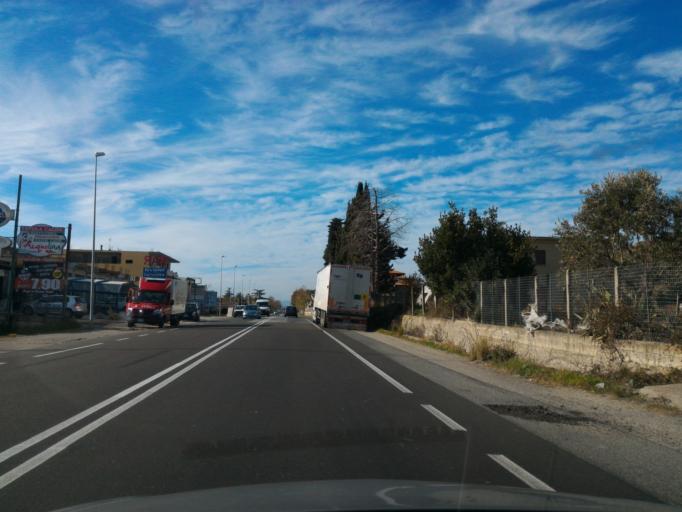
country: IT
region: Calabria
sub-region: Provincia di Catanzaro
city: Cropani Marina
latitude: 38.9210
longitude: 16.8009
